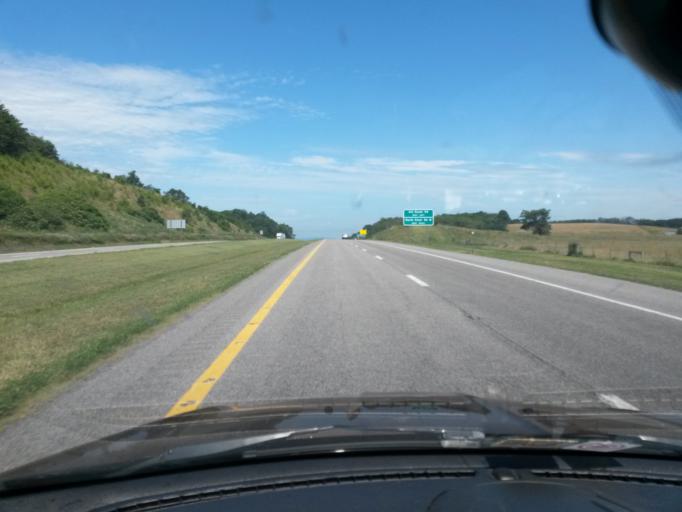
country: US
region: West Virginia
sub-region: Hardy County
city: Moorefield
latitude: 39.1005
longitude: -78.8373
